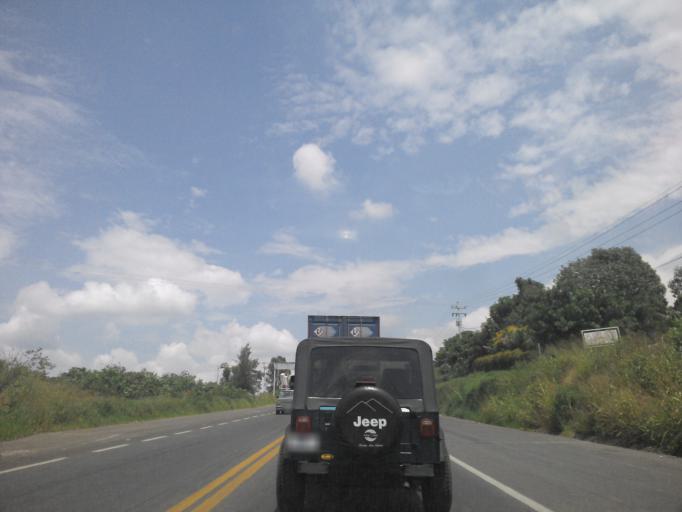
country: MX
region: Jalisco
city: Zapotlanejo
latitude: 20.6811
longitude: -103.0023
